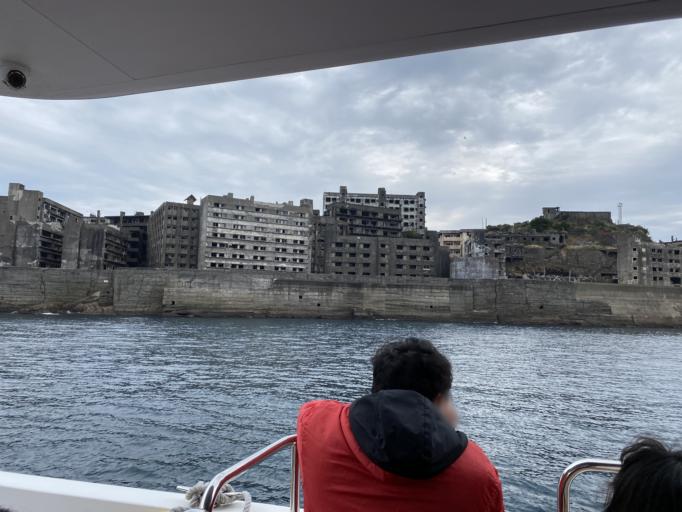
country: JP
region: Nagasaki
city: Nagasaki-shi
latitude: 32.6290
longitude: 129.7366
